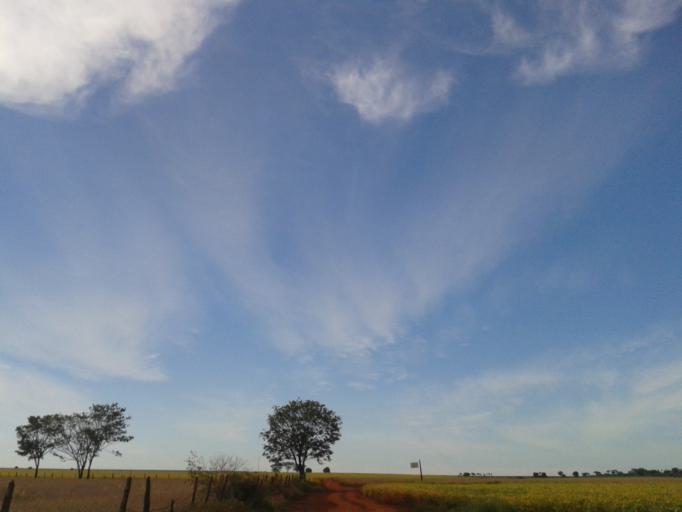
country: BR
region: Minas Gerais
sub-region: Capinopolis
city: Capinopolis
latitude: -18.6513
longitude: -49.7033
